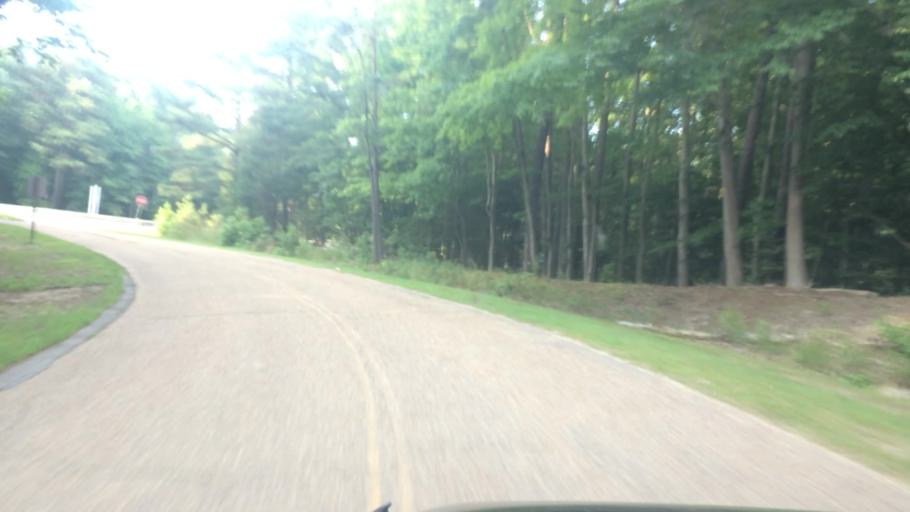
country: US
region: Virginia
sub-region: City of Williamsburg
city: Williamsburg
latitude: 37.2481
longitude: -76.6989
